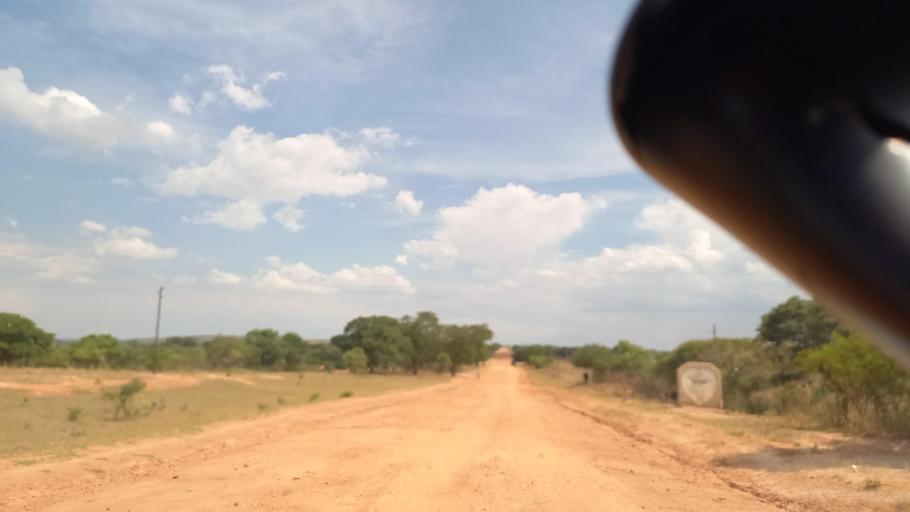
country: ZM
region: Lusaka
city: Kafue
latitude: -16.1319
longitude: 28.0483
